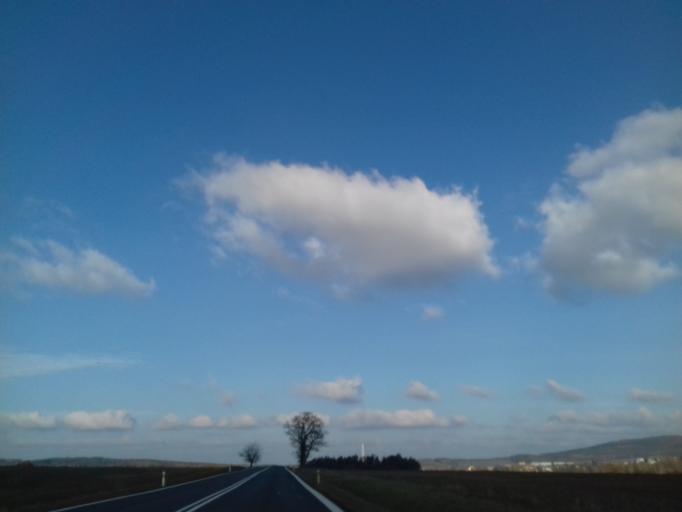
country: CZ
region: Plzensky
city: Holysov
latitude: 49.5796
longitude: 13.0809
